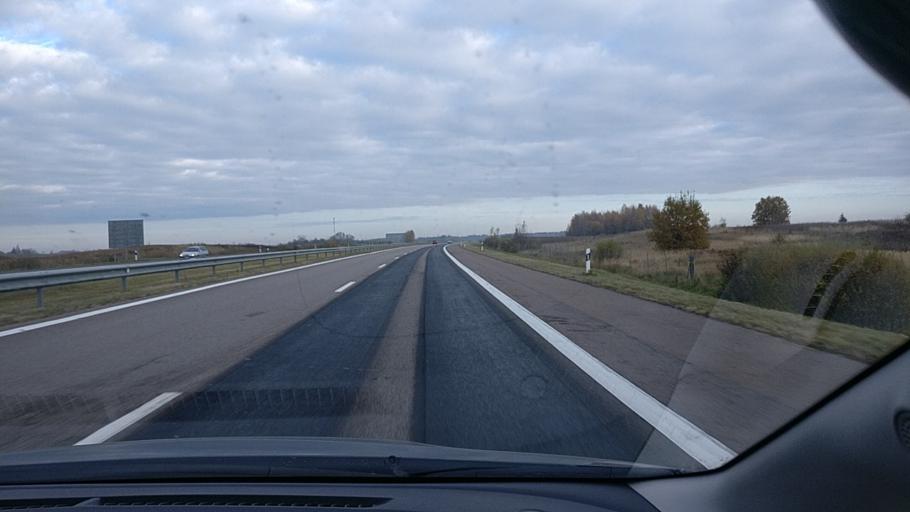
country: LT
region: Vilnius County
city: Ukmerge
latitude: 55.1862
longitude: 24.8113
